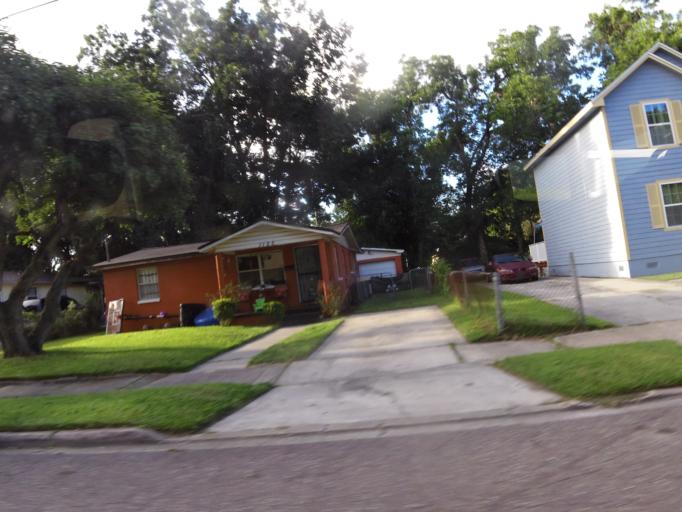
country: US
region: Florida
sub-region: Duval County
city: Jacksonville
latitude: 30.3596
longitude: -81.6718
